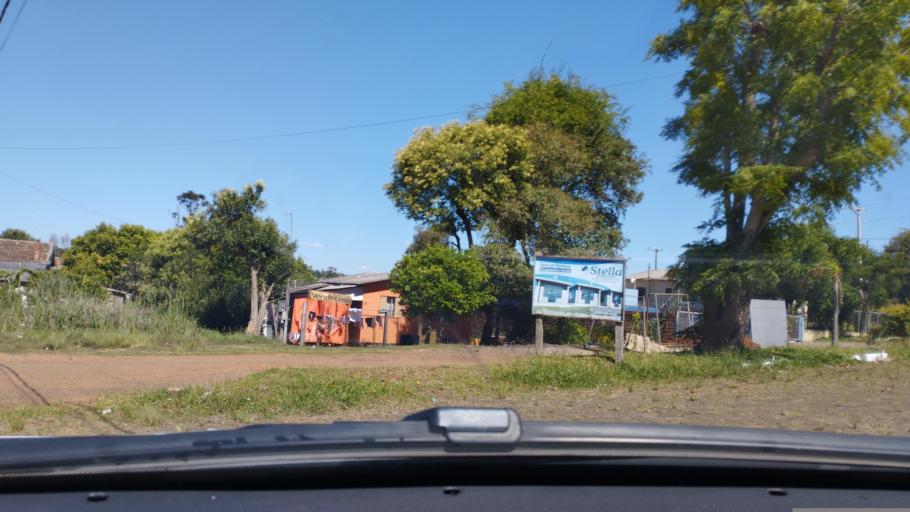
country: BR
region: Rio Grande do Sul
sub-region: Tupancireta
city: Tupancireta
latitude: -29.0903
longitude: -53.8346
